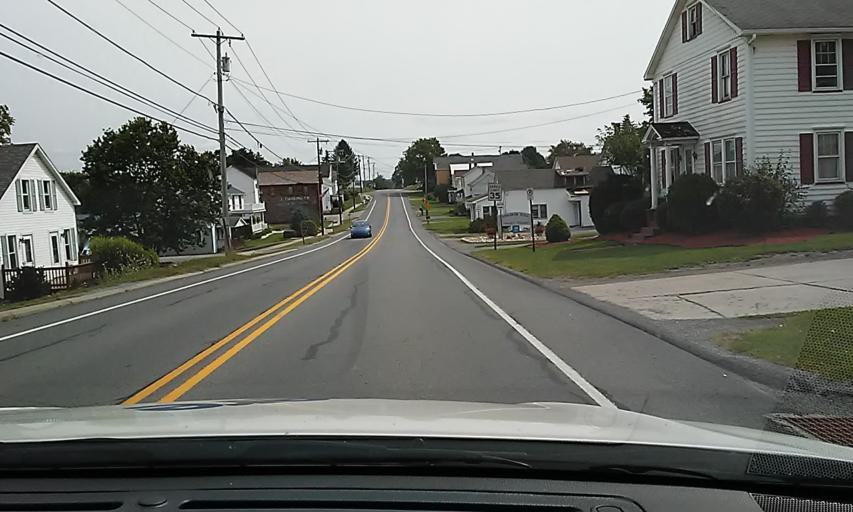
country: US
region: Pennsylvania
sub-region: Elk County
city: Saint Marys
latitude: 41.3621
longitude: -78.5998
